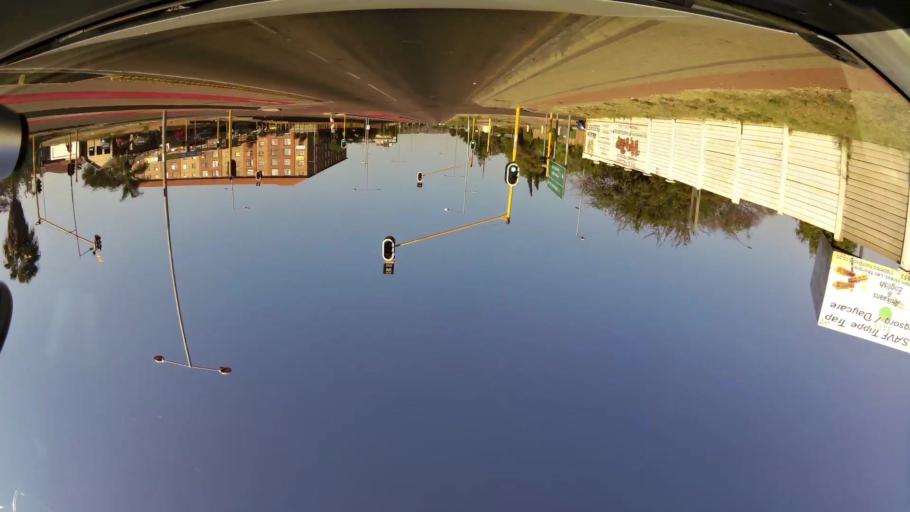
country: ZA
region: Gauteng
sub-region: City of Tshwane Metropolitan Municipality
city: Pretoria
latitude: -25.7097
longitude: 28.1866
